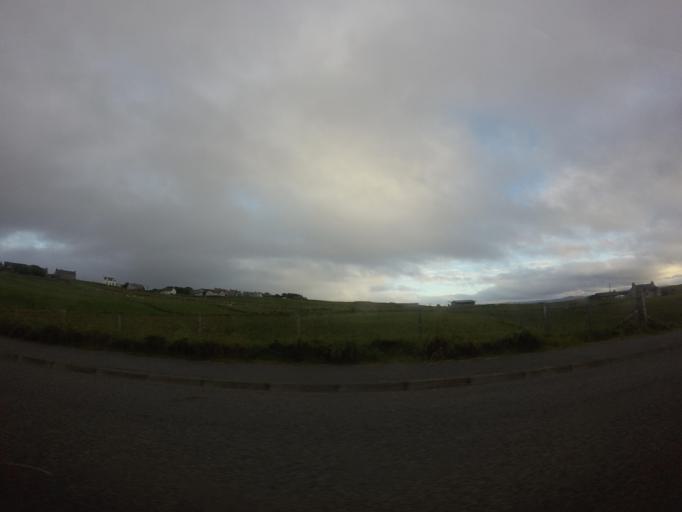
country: GB
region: Scotland
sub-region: Eilean Siar
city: Stornoway
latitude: 58.2052
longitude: -6.2723
